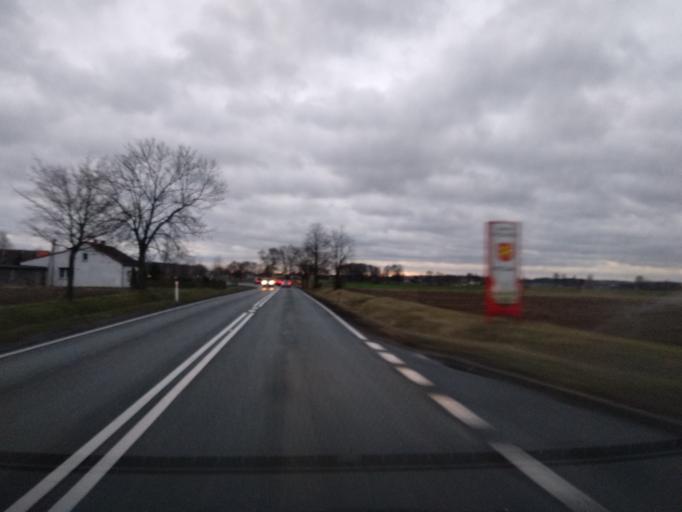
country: PL
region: Greater Poland Voivodeship
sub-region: Powiat koninski
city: Rychwal
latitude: 52.1022
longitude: 18.1670
